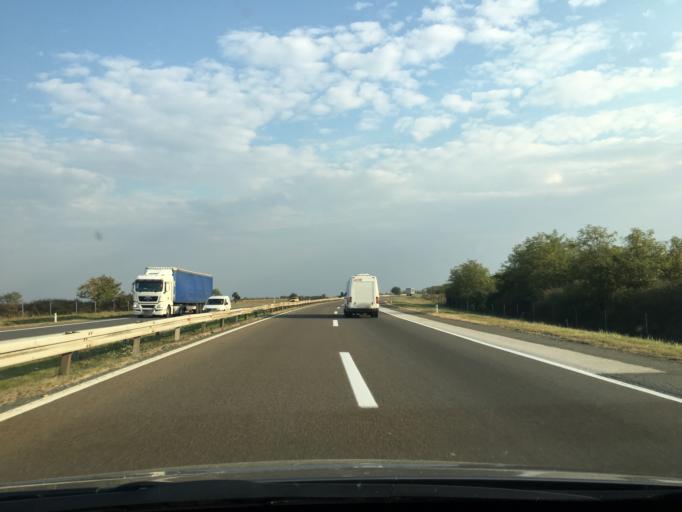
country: RS
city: Lugavcina
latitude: 44.5374
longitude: 20.9985
